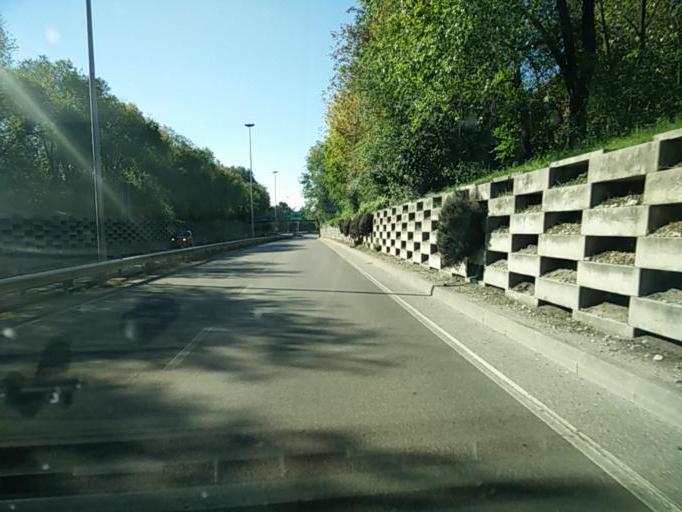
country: IT
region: Veneto
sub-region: Provincia di Verona
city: Verona
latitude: 45.4297
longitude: 10.9742
